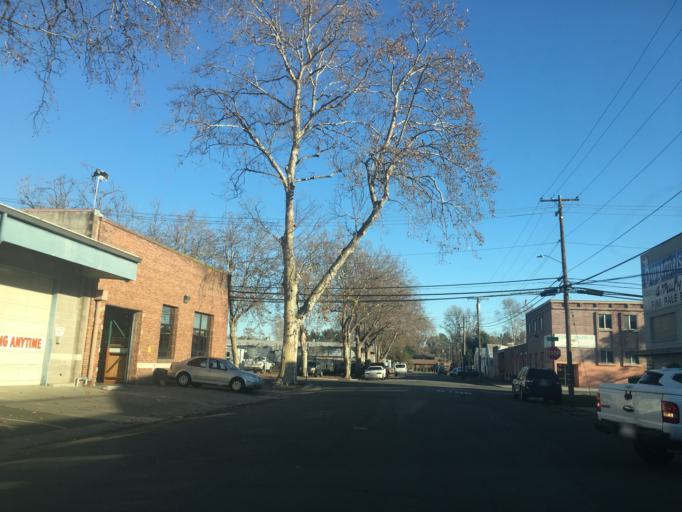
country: US
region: California
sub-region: Sacramento County
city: Sacramento
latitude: 38.5646
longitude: -121.5083
